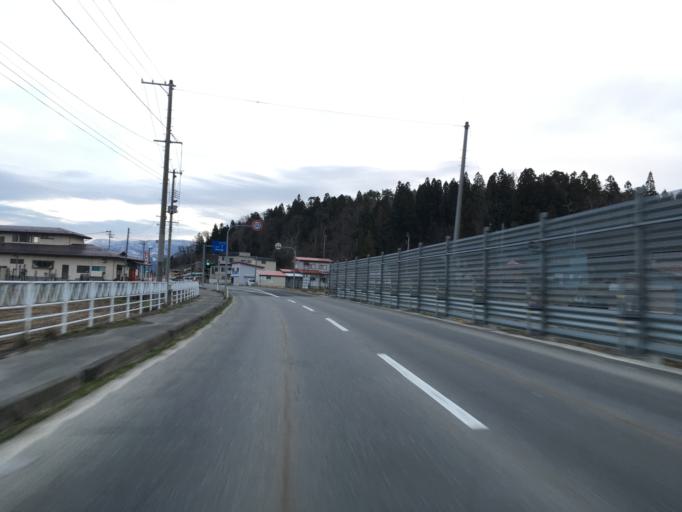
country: JP
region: Yamagata
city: Yonezawa
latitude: 37.9463
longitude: 140.0728
